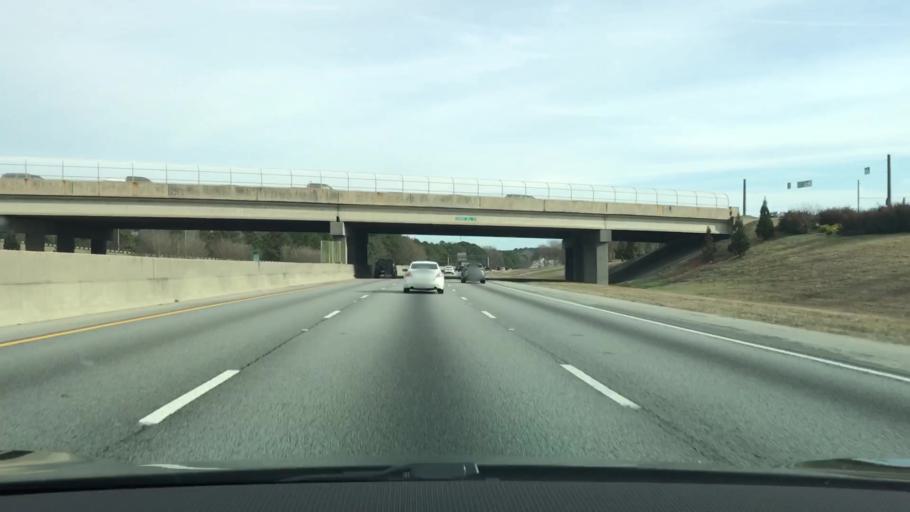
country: US
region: Georgia
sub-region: DeKalb County
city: Lithonia
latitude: 33.7005
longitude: -84.0895
